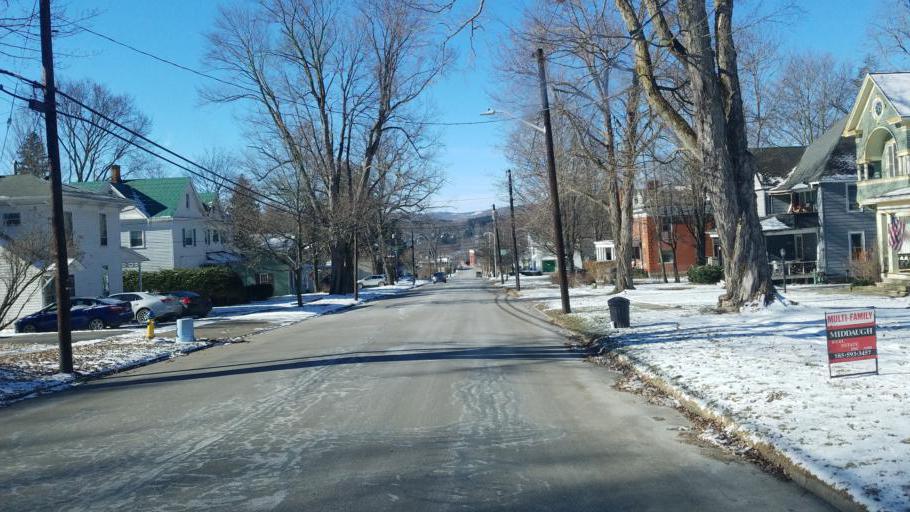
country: US
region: New York
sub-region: Allegany County
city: Wellsville
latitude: 42.1249
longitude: -77.9436
